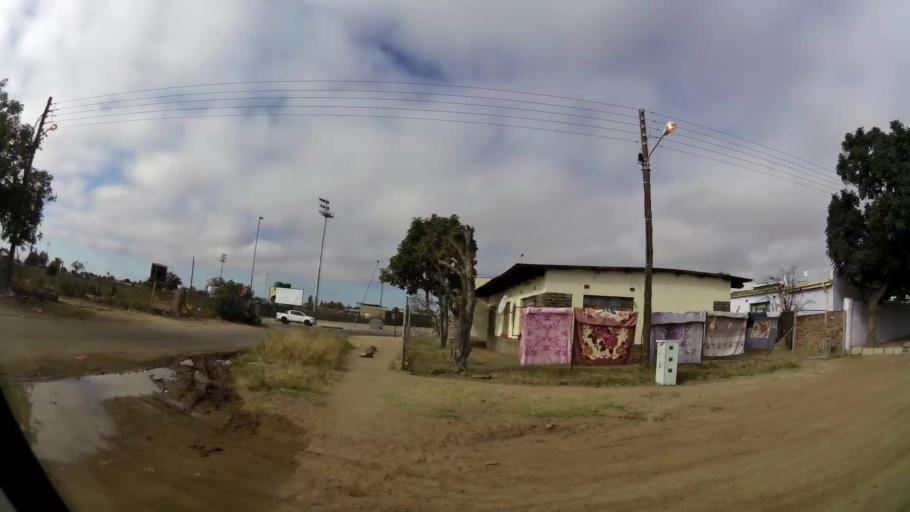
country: ZA
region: Limpopo
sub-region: Capricorn District Municipality
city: Polokwane
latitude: -23.8535
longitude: 29.3876
